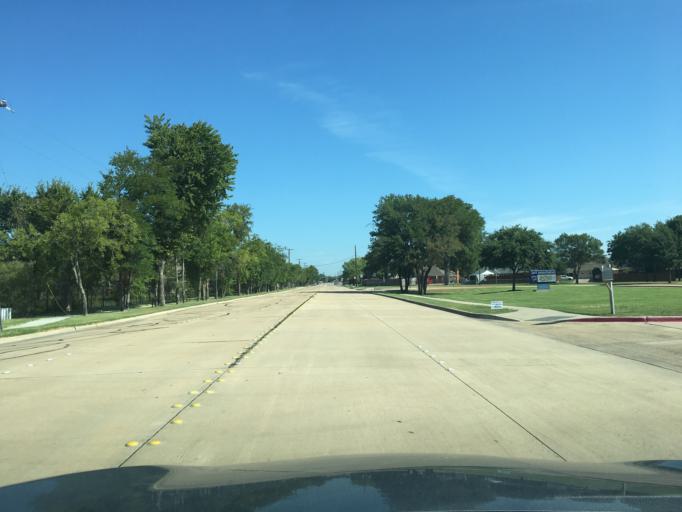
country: US
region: Texas
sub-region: Dallas County
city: Sachse
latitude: 32.9667
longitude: -96.6011
